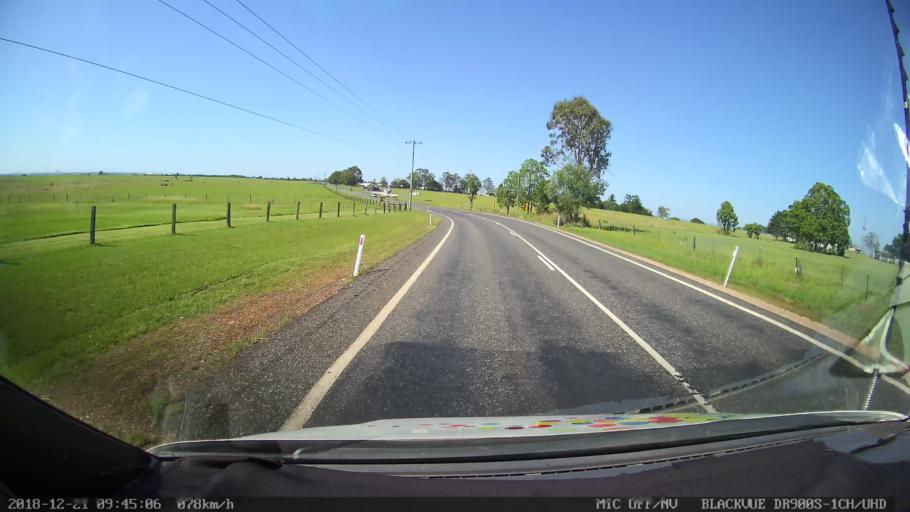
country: AU
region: New South Wales
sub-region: Clarence Valley
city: Grafton
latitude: -29.6247
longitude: 152.9295
